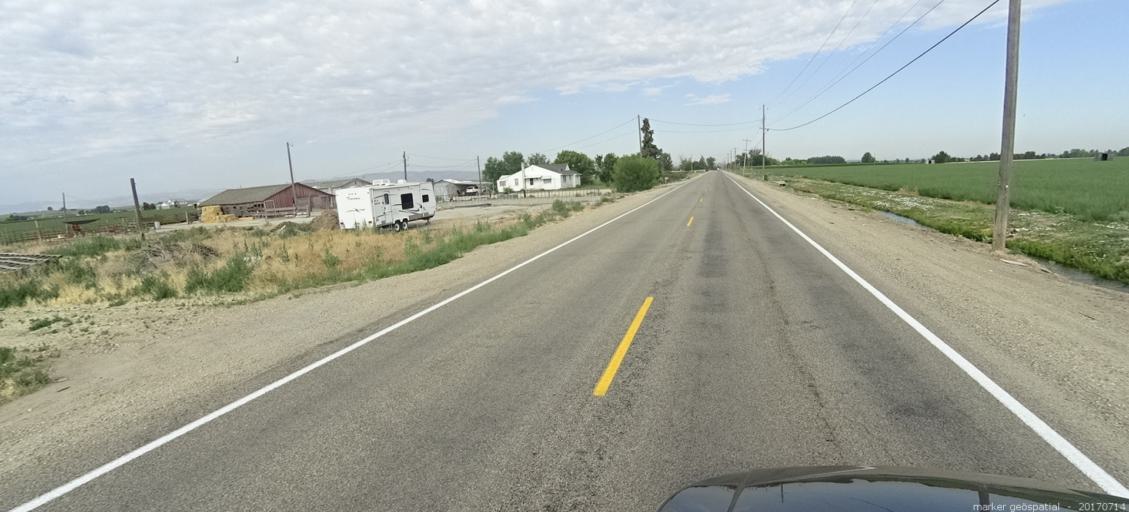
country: US
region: Idaho
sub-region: Ada County
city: Kuna
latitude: 43.4883
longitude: -116.4574
